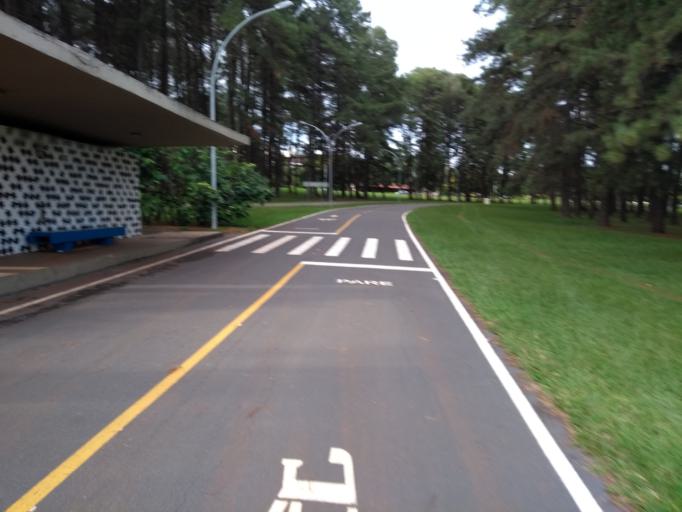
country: BR
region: Federal District
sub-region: Brasilia
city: Brasilia
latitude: -15.8068
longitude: -47.9227
